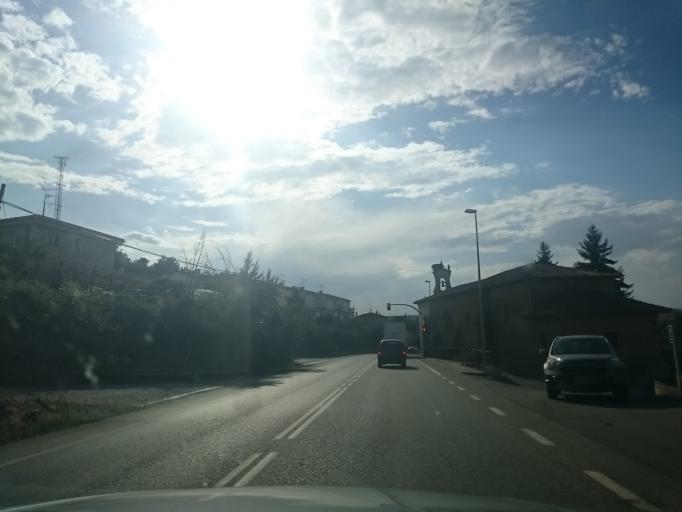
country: ES
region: Castille and Leon
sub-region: Provincia de Burgos
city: Belorado
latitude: 42.4180
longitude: -3.1868
